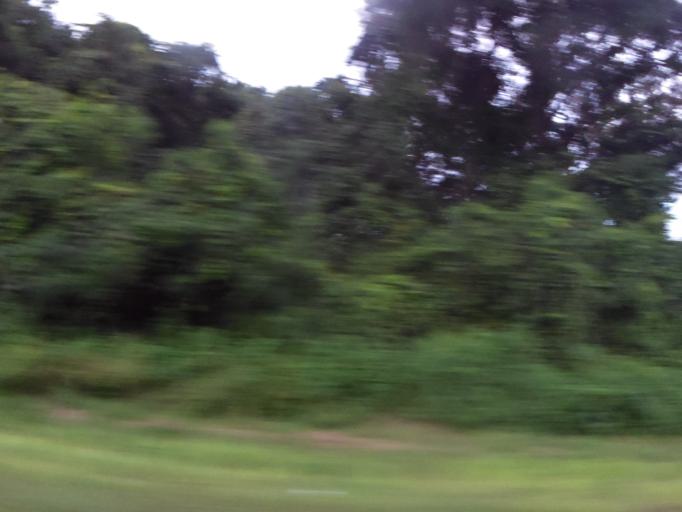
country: US
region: Florida
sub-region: Nassau County
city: Fernandina Beach
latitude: 30.6036
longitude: -81.4481
